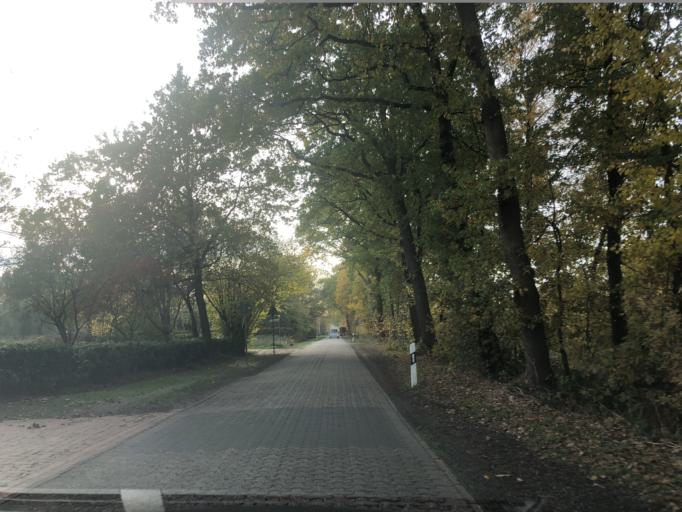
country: DE
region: Lower Saxony
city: Edewecht
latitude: 53.0956
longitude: 8.0871
